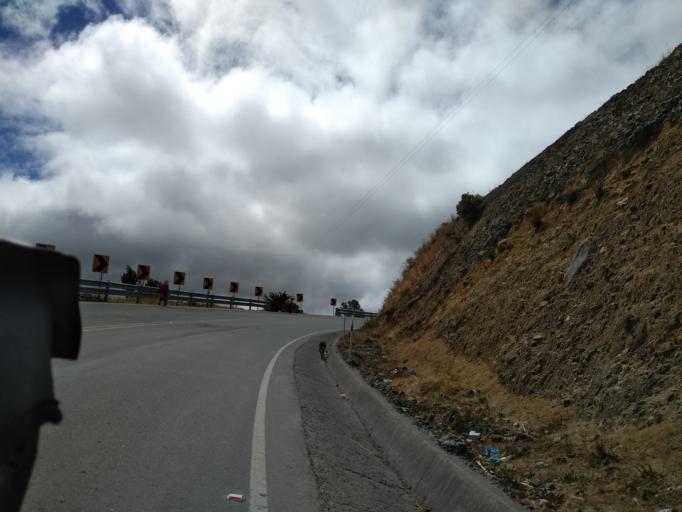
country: EC
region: Cotopaxi
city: Pujili
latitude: -0.9475
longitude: -78.9194
